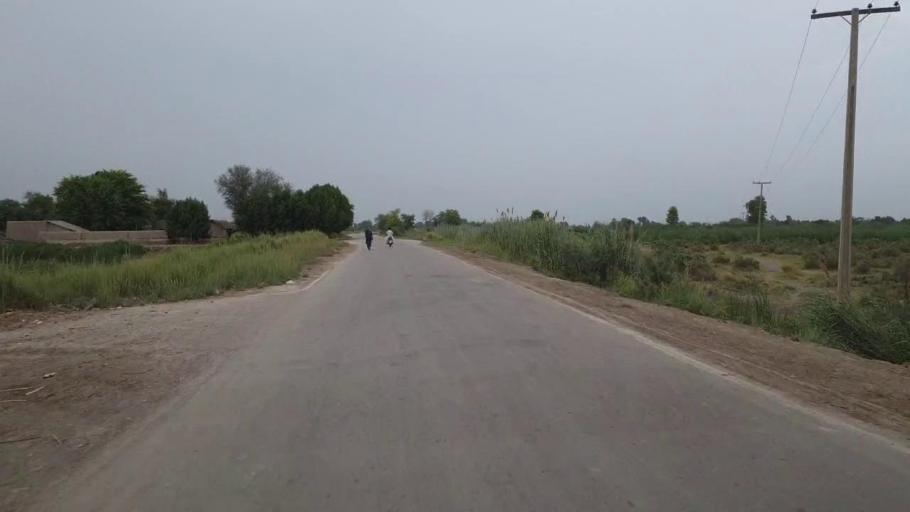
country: PK
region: Sindh
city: Bandhi
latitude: 26.5392
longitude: 68.2195
